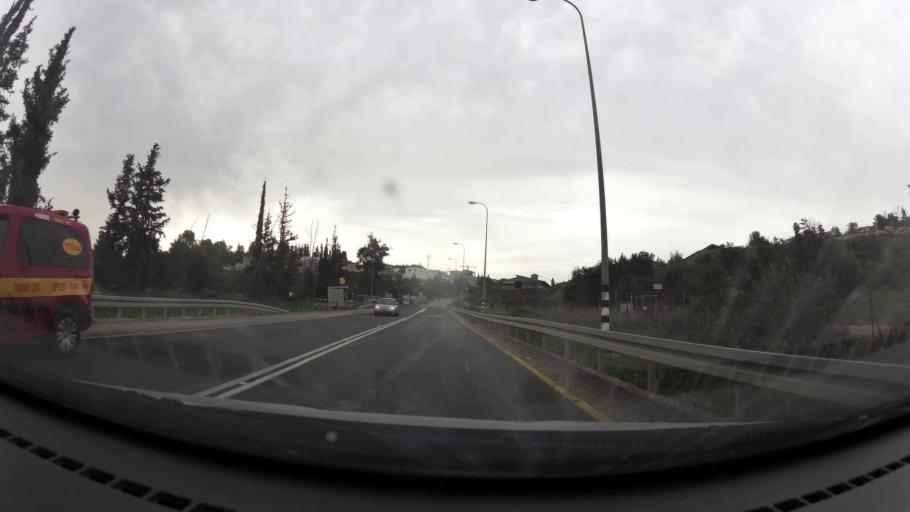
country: IL
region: Jerusalem
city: Bet Shemesh
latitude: 31.6754
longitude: 35.0108
